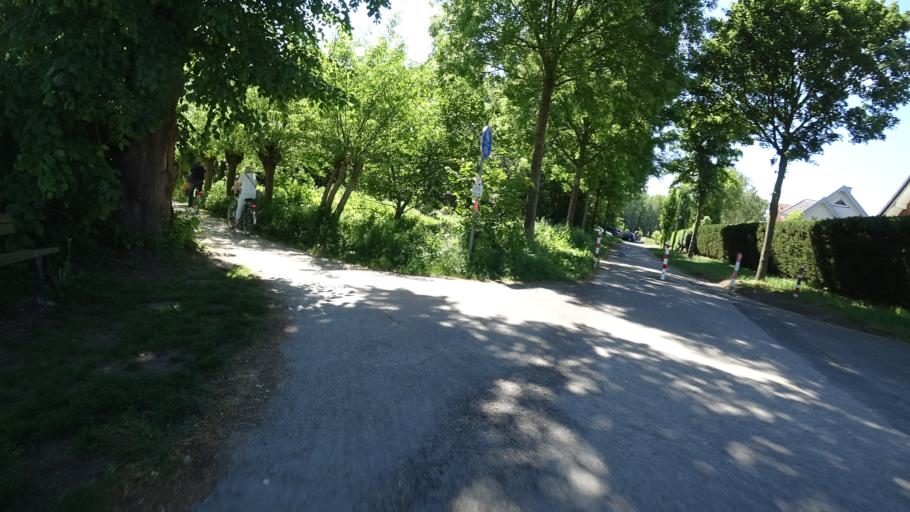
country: DE
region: North Rhine-Westphalia
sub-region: Regierungsbezirk Detmold
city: Rheda-Wiedenbruck
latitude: 51.8296
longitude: 8.3305
